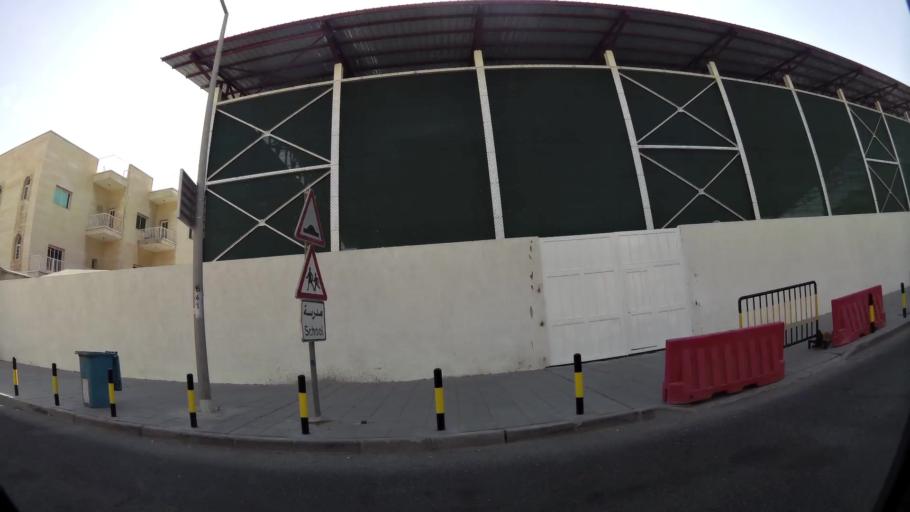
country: KW
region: Muhafazat Hawalli
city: Ar Rumaythiyah
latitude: 29.3022
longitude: 48.0643
